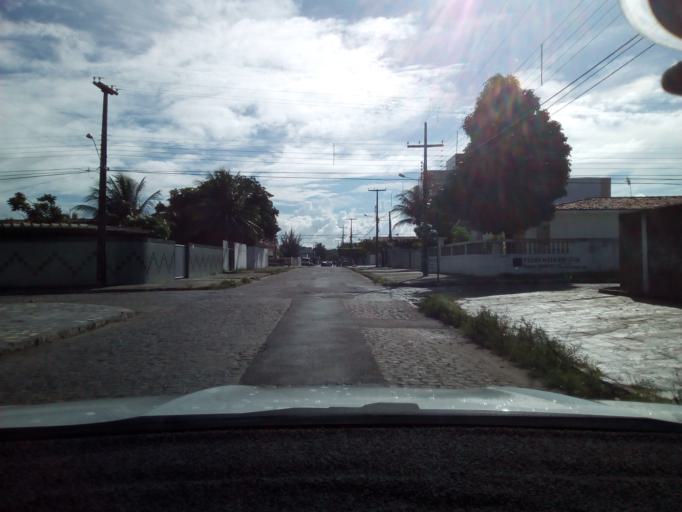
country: BR
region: Paraiba
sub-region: Joao Pessoa
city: Joao Pessoa
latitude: -7.1614
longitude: -34.8734
